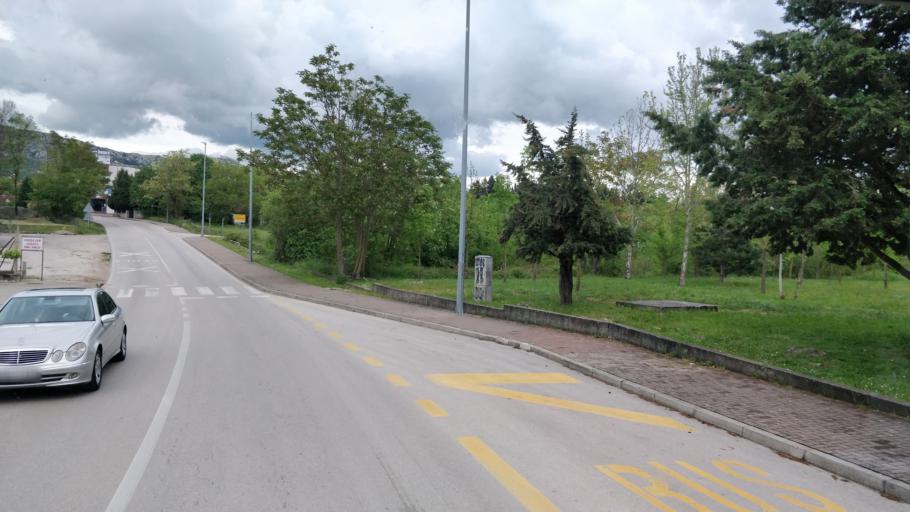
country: BA
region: Federation of Bosnia and Herzegovina
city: Ljubuski
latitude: 43.1836
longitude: 17.5271
